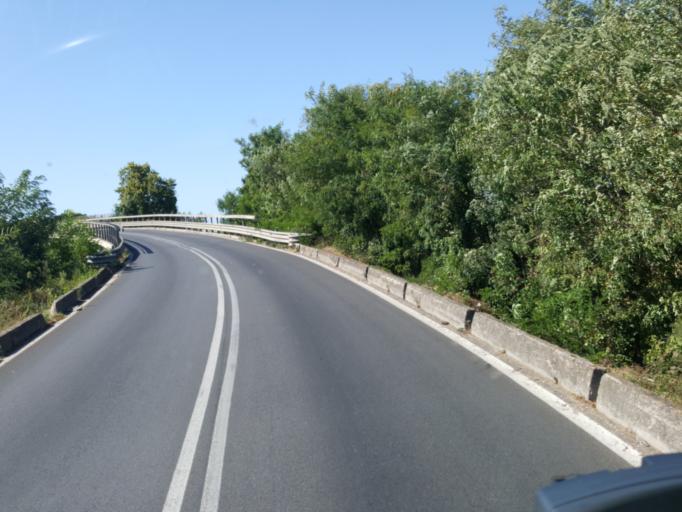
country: IT
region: Latium
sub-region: Citta metropolitana di Roma Capitale
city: Anzio
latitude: 41.5143
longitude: 12.6307
